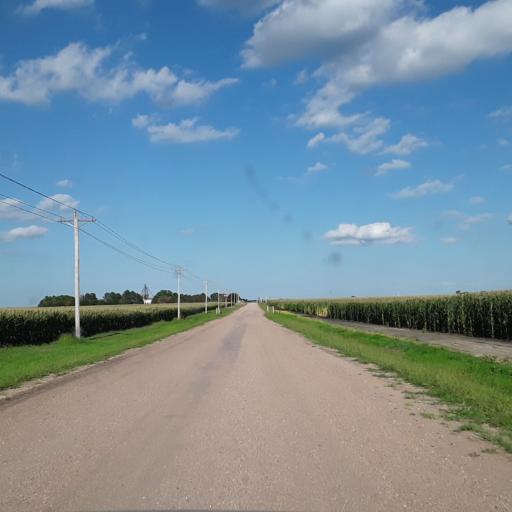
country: US
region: Nebraska
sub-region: Hall County
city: Wood River
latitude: 40.9168
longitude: -98.5958
